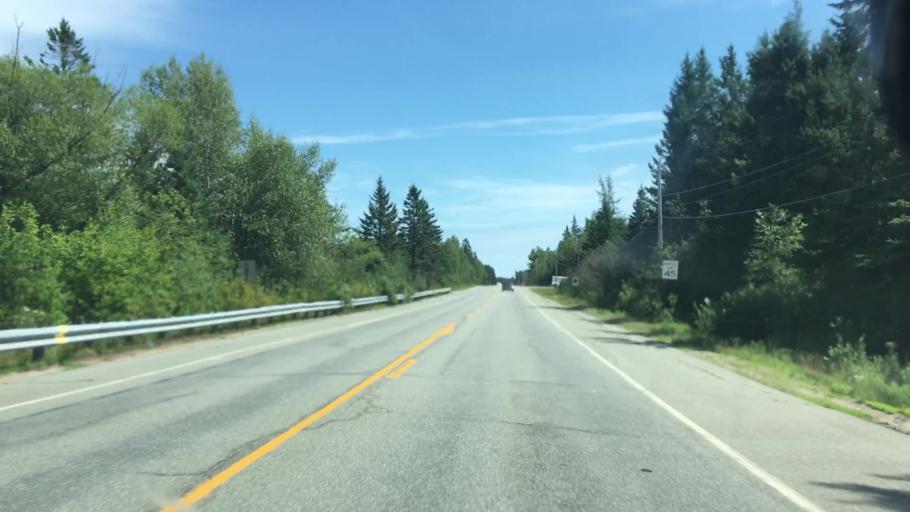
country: US
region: Maine
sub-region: Washington County
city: Eastport
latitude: 44.9696
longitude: -67.0736
